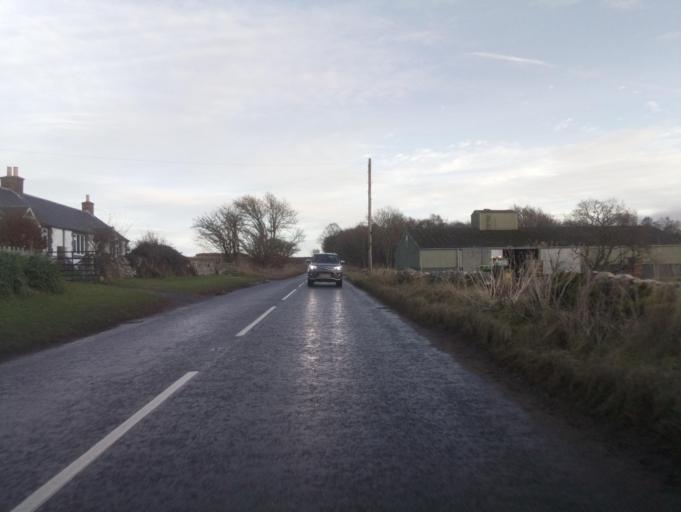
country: GB
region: Scotland
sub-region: Angus
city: Forfar
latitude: 56.5866
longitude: -2.8628
